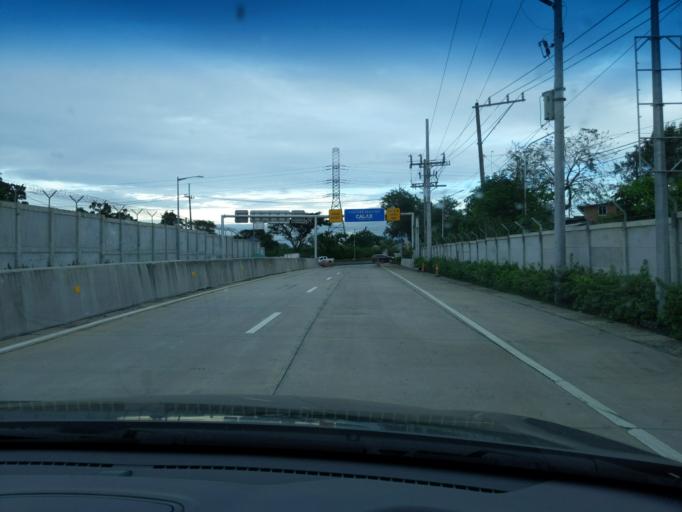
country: PH
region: Calabarzon
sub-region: Province of Cavite
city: Puting Kahoy
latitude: 14.2293
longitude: 121.0495
